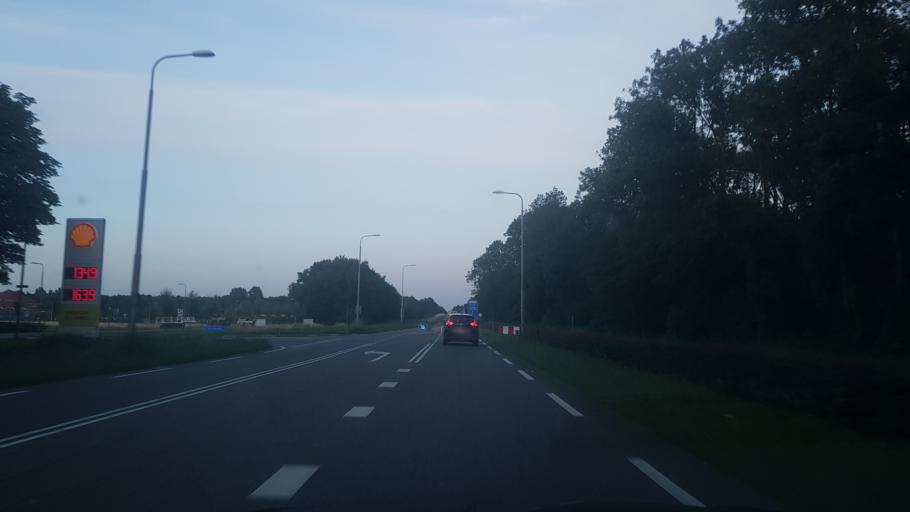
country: NL
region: Flevoland
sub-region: Gemeente Noordoostpolder
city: Emmeloord
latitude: 52.7255
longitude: 5.7605
